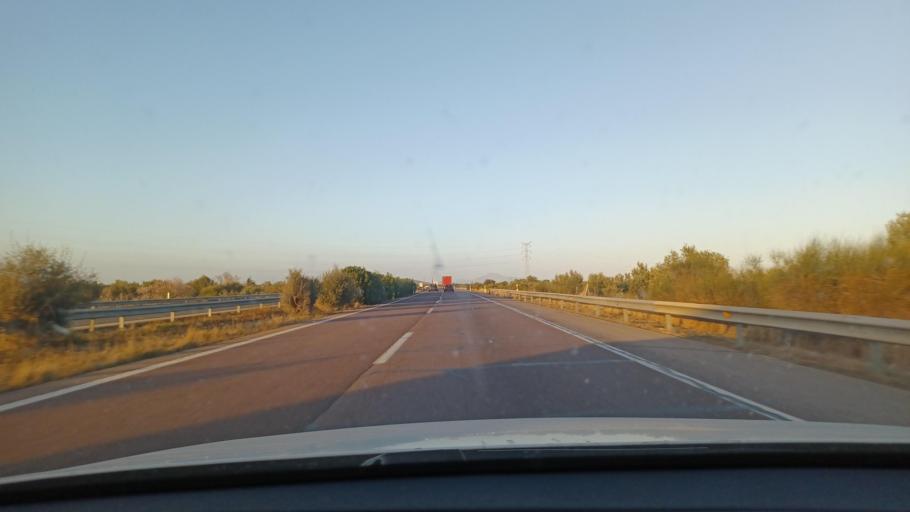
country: ES
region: Valencia
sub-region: Provincia de Castello
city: Benicarlo
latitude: 40.4270
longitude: 0.3833
